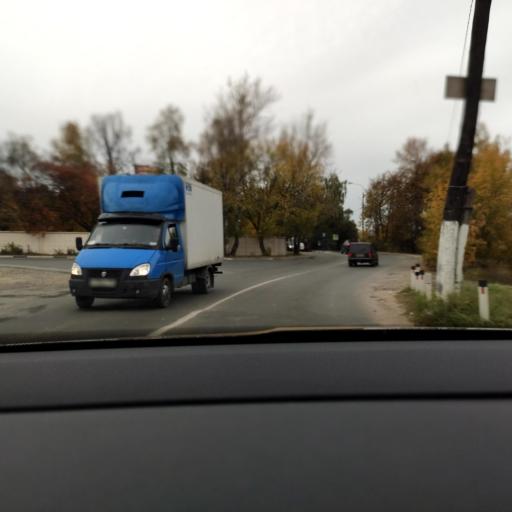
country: RU
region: Moskovskaya
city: Ivanteyevka
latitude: 55.9656
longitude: 37.9425
